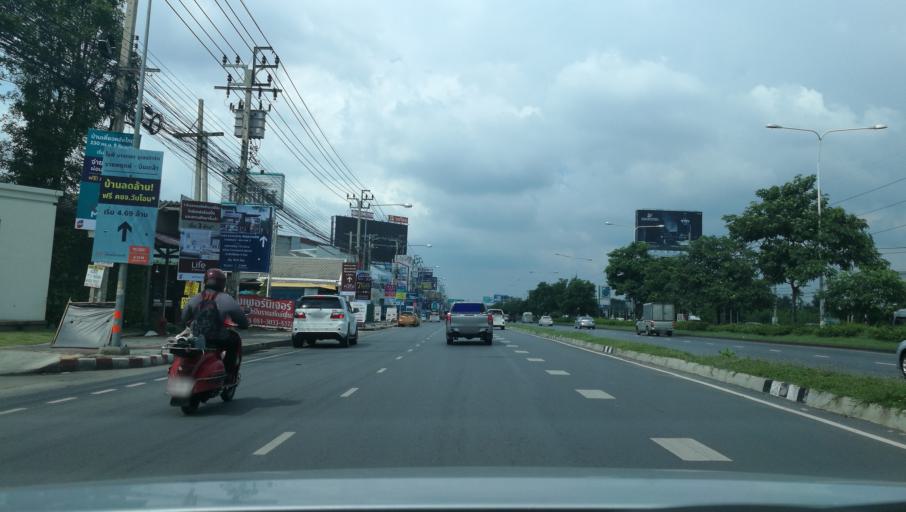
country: TH
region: Nonthaburi
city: Bang Kruai
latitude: 13.8114
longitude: 100.4494
